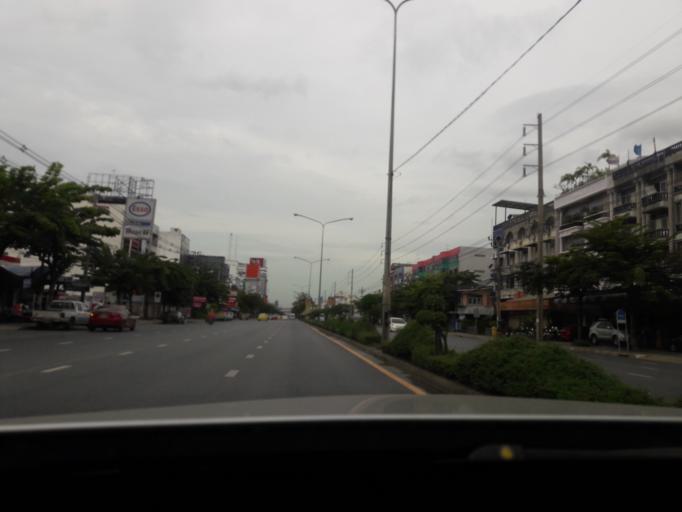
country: TH
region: Bangkok
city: Bang Phlat
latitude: 13.7867
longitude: 100.4881
